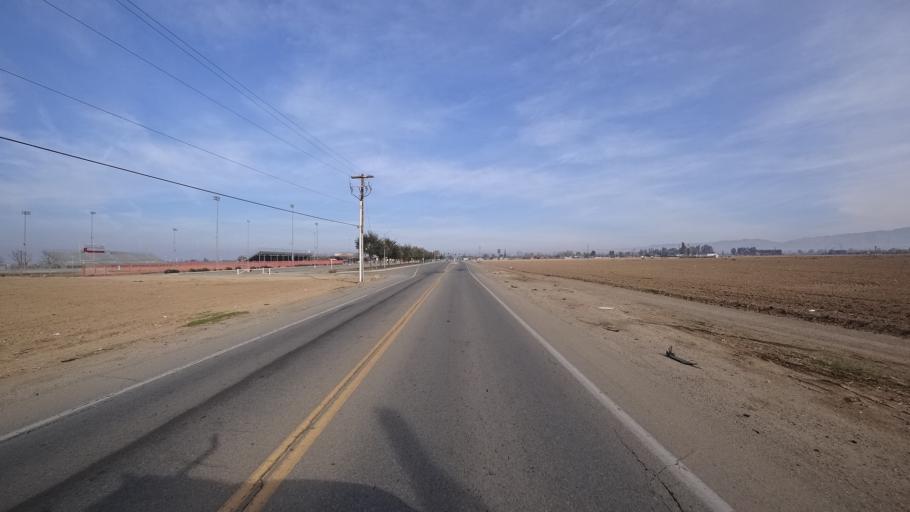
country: US
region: California
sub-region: Kern County
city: Lamont
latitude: 35.3336
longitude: -118.9320
